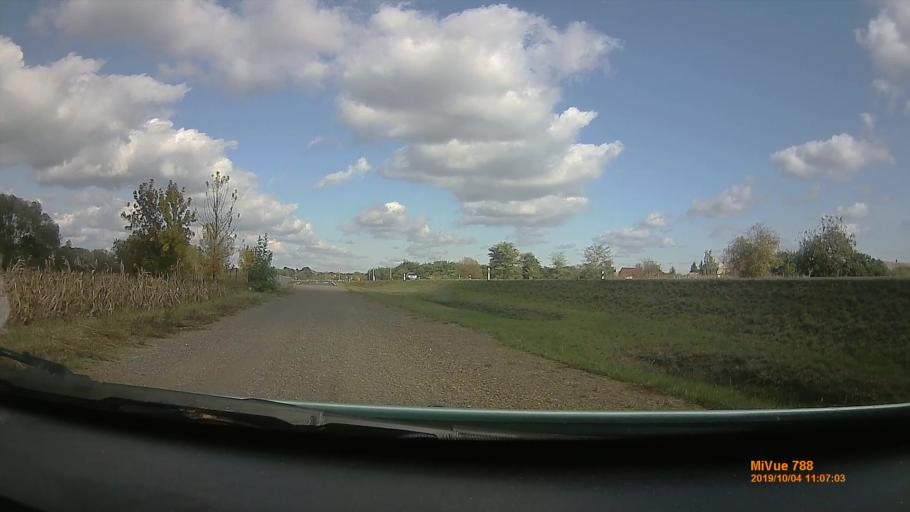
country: HU
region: Szabolcs-Szatmar-Bereg
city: Nyirtelek
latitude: 47.9942
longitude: 21.6736
